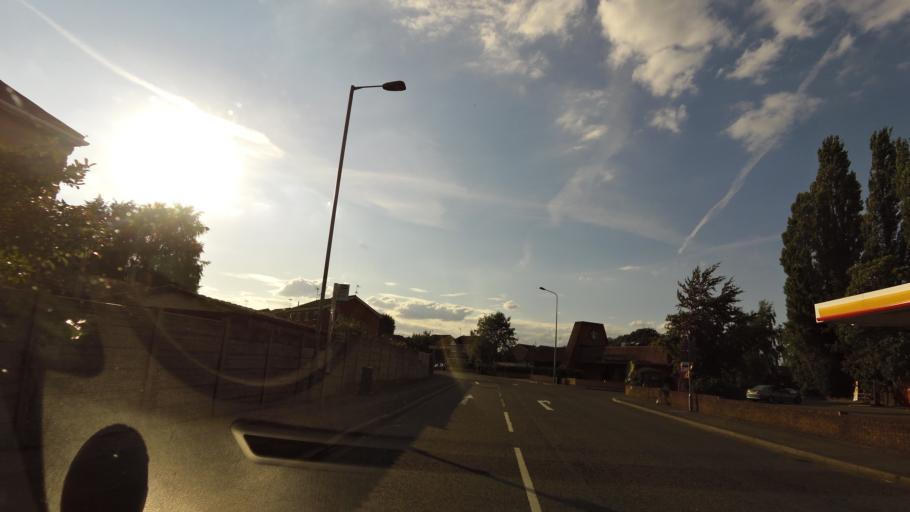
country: GB
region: England
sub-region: Nottinghamshire
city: Worksop
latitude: 53.3026
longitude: -1.1377
